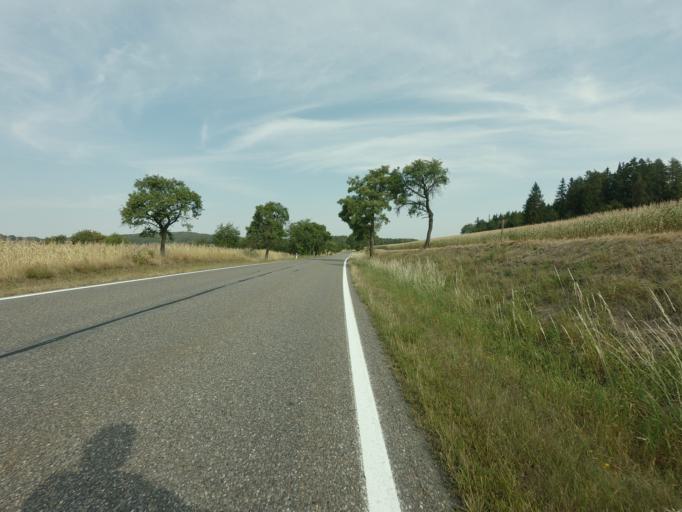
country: CZ
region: Central Bohemia
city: Petrovice
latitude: 49.5195
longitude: 14.3562
